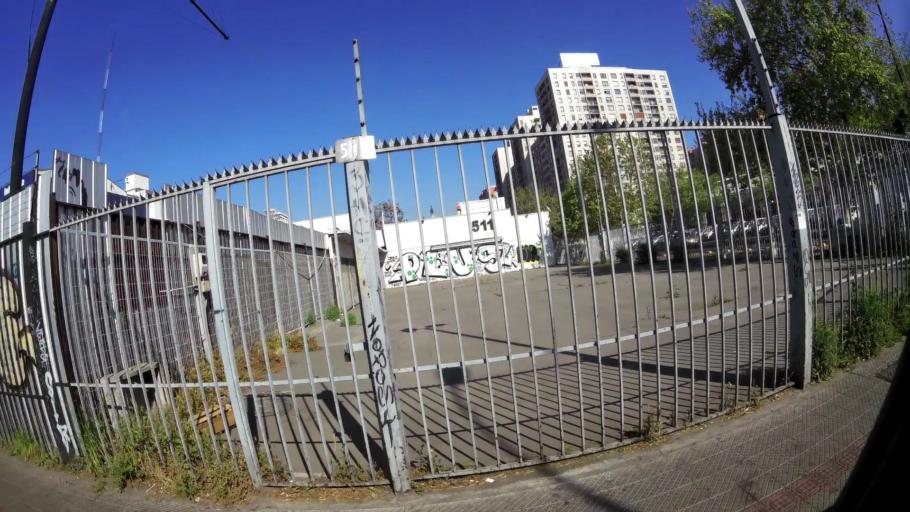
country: CL
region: Santiago Metropolitan
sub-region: Provincia de Santiago
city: Santiago
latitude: -33.4507
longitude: -70.6444
